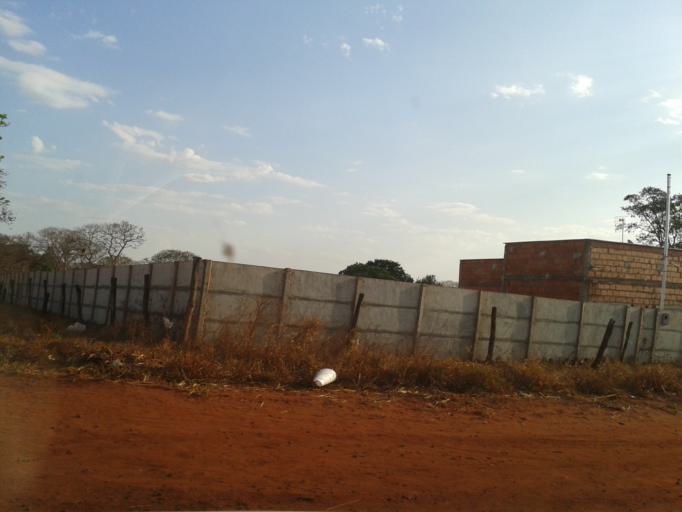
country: BR
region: Minas Gerais
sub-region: Ituiutaba
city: Ituiutaba
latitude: -18.9994
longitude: -49.4351
